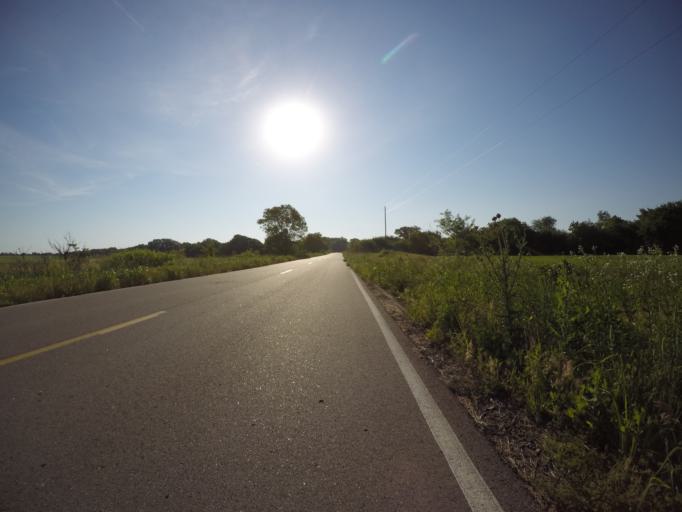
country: US
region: Nebraska
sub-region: Gage County
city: Wymore
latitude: 40.1028
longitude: -96.5058
